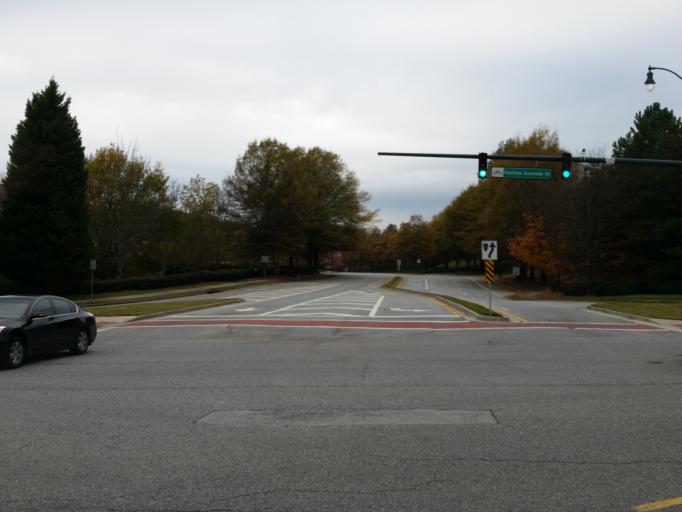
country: US
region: Georgia
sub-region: DeKalb County
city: Dunwoody
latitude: 33.9275
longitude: -84.3515
